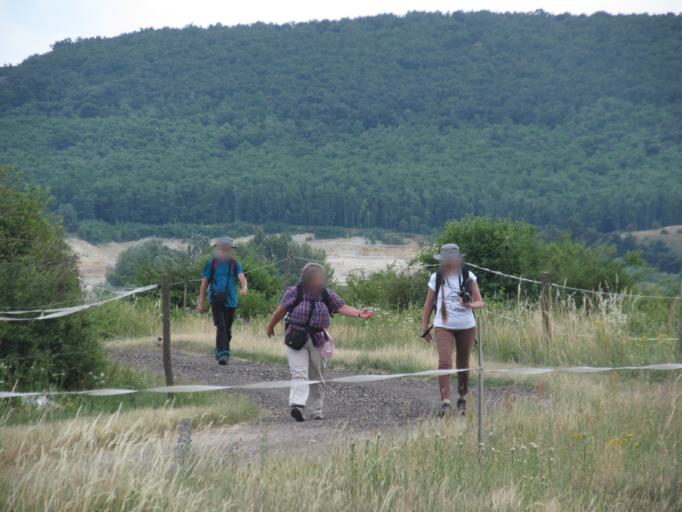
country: HU
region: Veszprem
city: Badacsonytomaj
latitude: 46.8460
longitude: 17.5511
